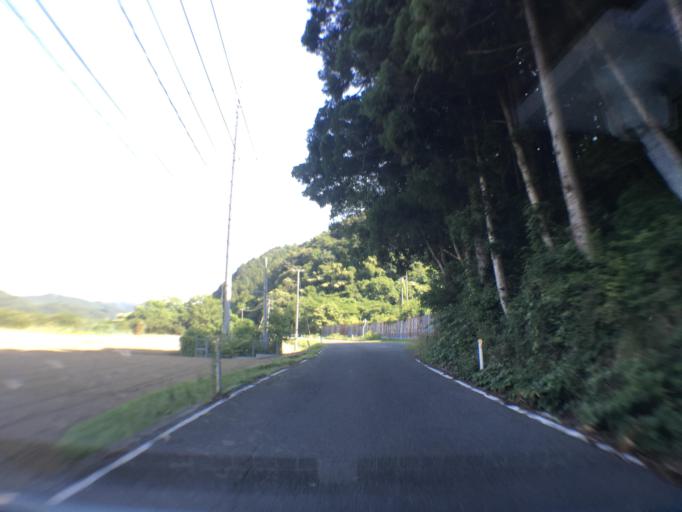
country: JP
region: Miyagi
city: Wakuya
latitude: 38.6354
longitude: 141.2842
